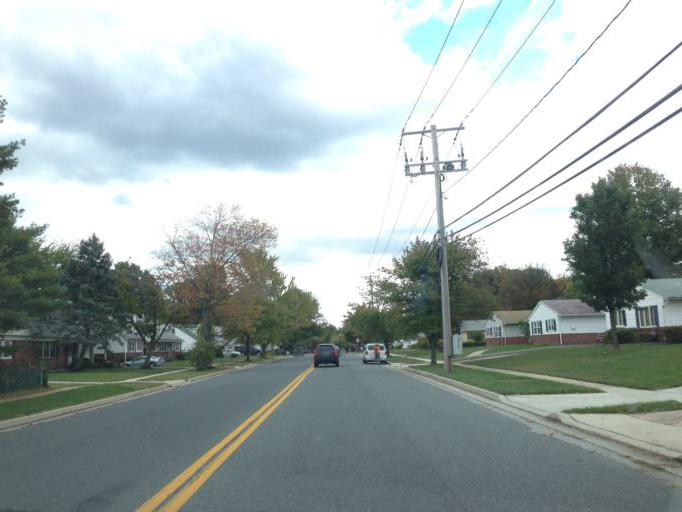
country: US
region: Maryland
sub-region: Baltimore County
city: Woodlawn
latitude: 39.3107
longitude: -76.7636
